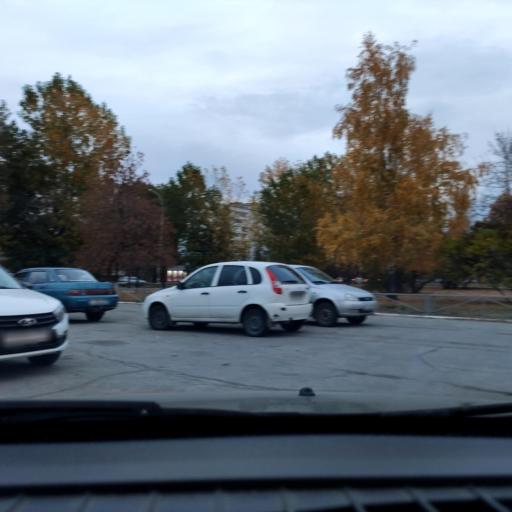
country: RU
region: Samara
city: Tol'yatti
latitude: 53.5073
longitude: 49.2621
